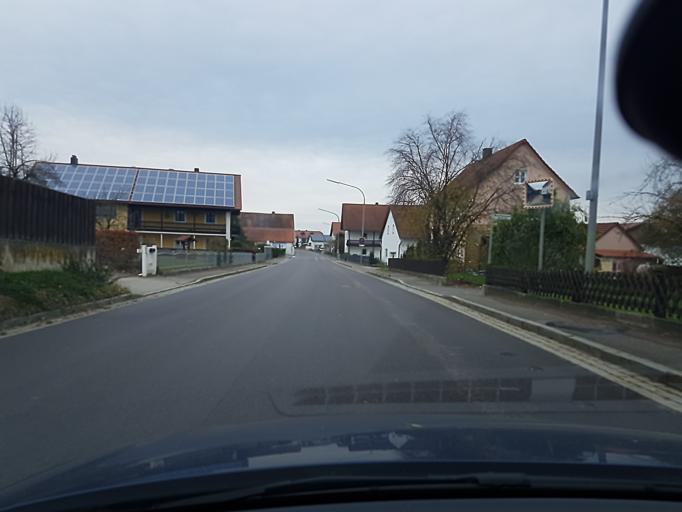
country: DE
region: Bavaria
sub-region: Upper Palatinate
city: Schierling
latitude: 48.8127
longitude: 12.1707
